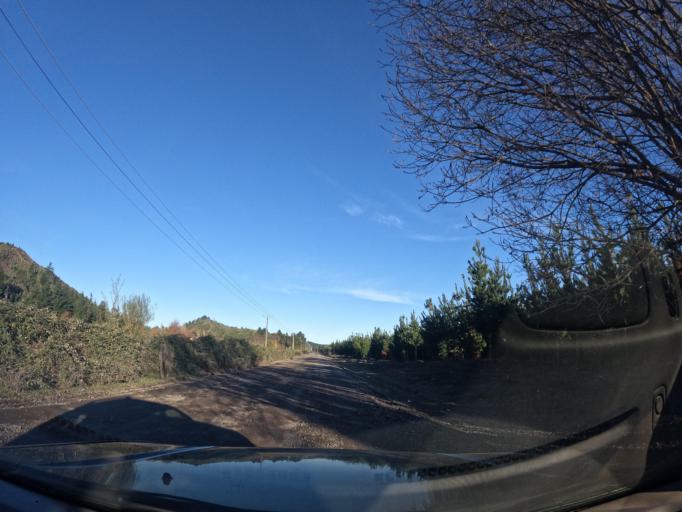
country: CL
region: Biobio
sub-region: Provincia de Concepcion
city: Chiguayante
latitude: -37.0696
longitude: -72.9455
